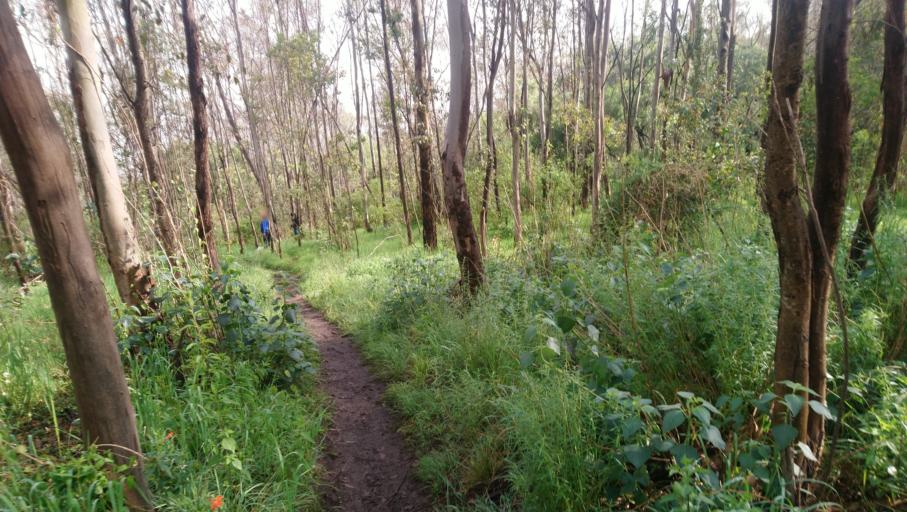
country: MX
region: Mexico
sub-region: Tultitlan
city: Ampliacion San Mateo (Colonia Solidaridad)
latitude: 19.6083
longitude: -99.1236
